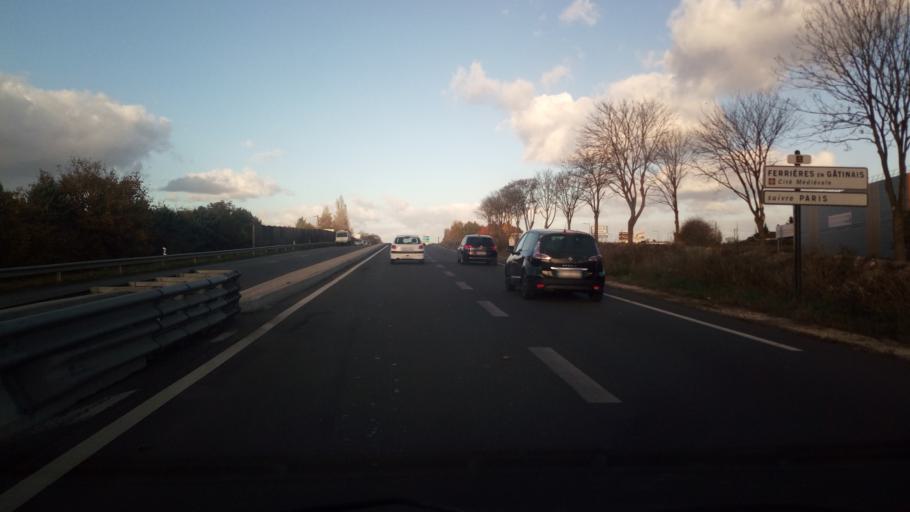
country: FR
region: Centre
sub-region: Departement du Loiret
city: Villemandeur
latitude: 47.9739
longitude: 2.7381
